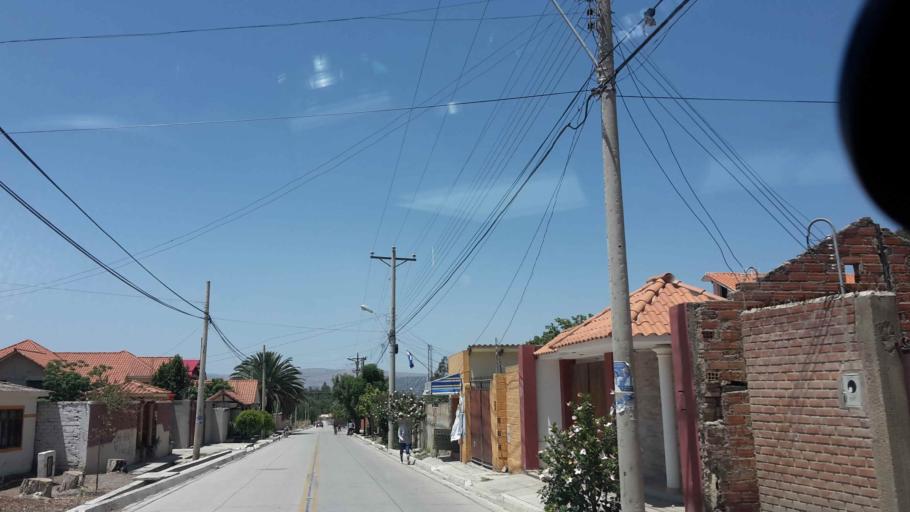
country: BO
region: Cochabamba
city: Cochabamba
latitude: -17.3518
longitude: -66.2064
